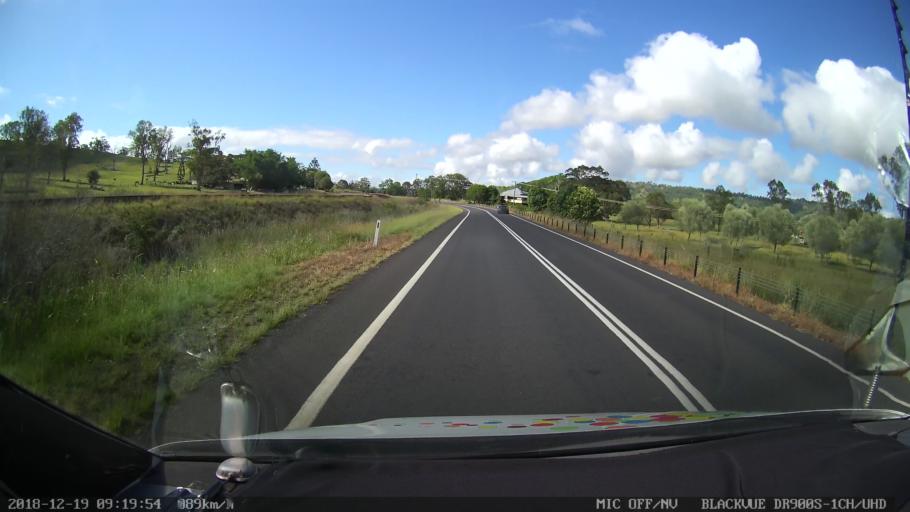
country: AU
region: New South Wales
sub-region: Kyogle
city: Kyogle
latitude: -28.5660
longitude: 152.9779
